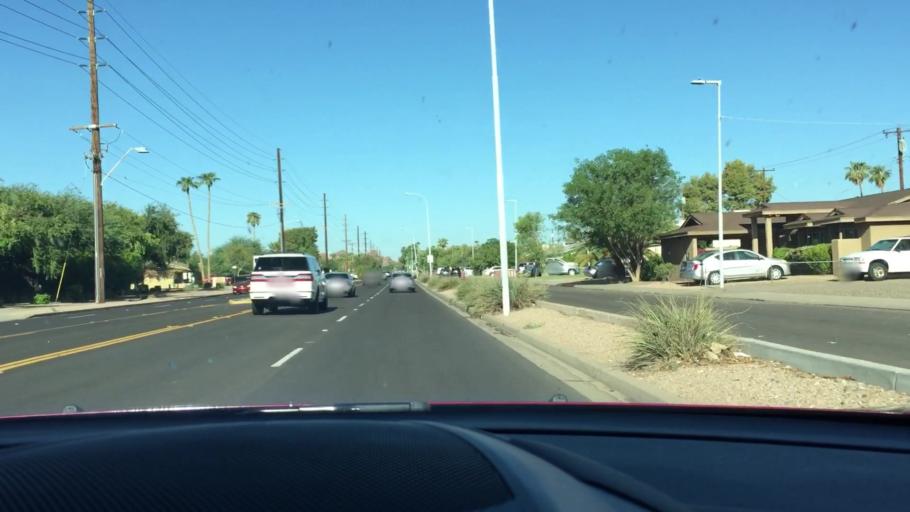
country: US
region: Arizona
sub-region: Maricopa County
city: Tempe
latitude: 33.4482
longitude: -111.9218
